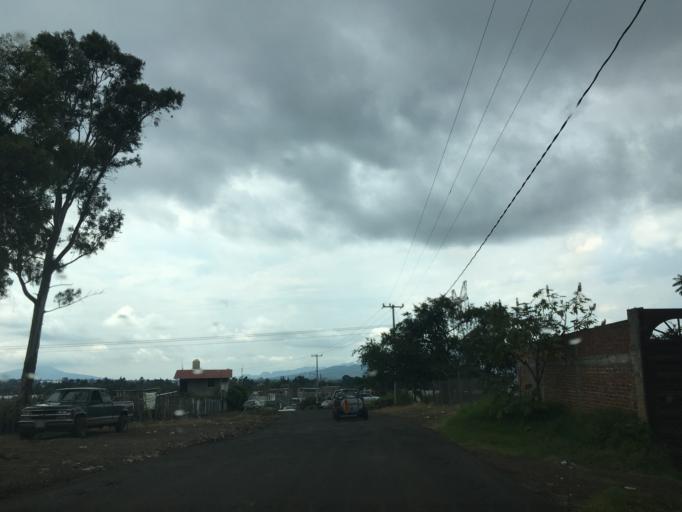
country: MX
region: Michoacan
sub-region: Periban
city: Gildardo Magana (Los Angeles)
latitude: 19.5795
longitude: -102.4509
